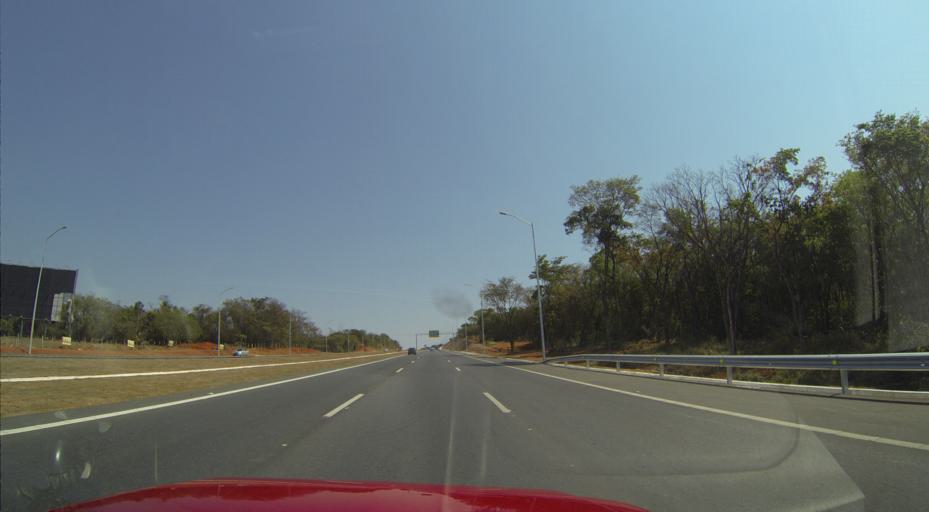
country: BR
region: Minas Gerais
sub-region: Vespasiano
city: Vespasiano
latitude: -19.6573
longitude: -43.9415
